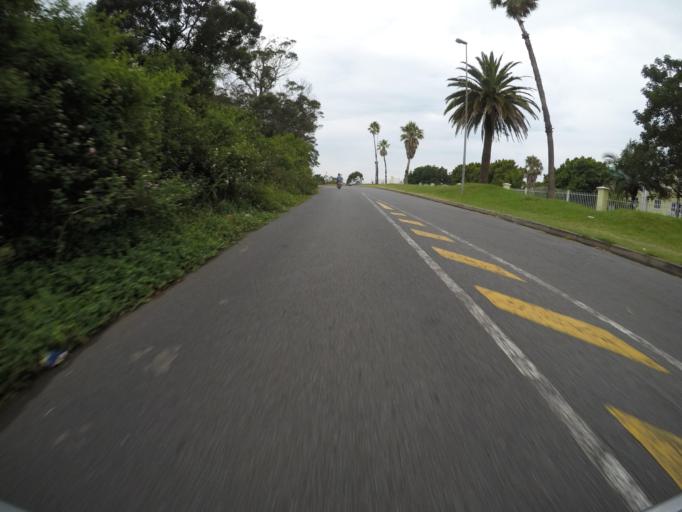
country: ZA
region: Eastern Cape
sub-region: Buffalo City Metropolitan Municipality
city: East London
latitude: -32.9700
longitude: 27.9014
